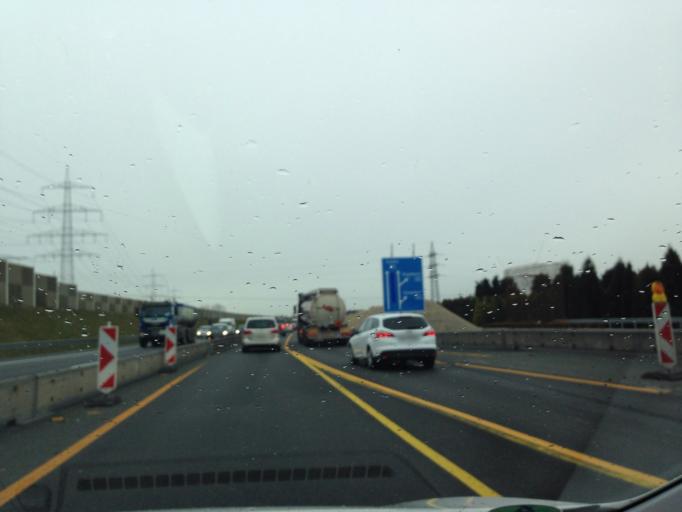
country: DE
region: North Rhine-Westphalia
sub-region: Regierungsbezirk Dusseldorf
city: Kaarst
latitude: 51.2218
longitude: 6.6400
